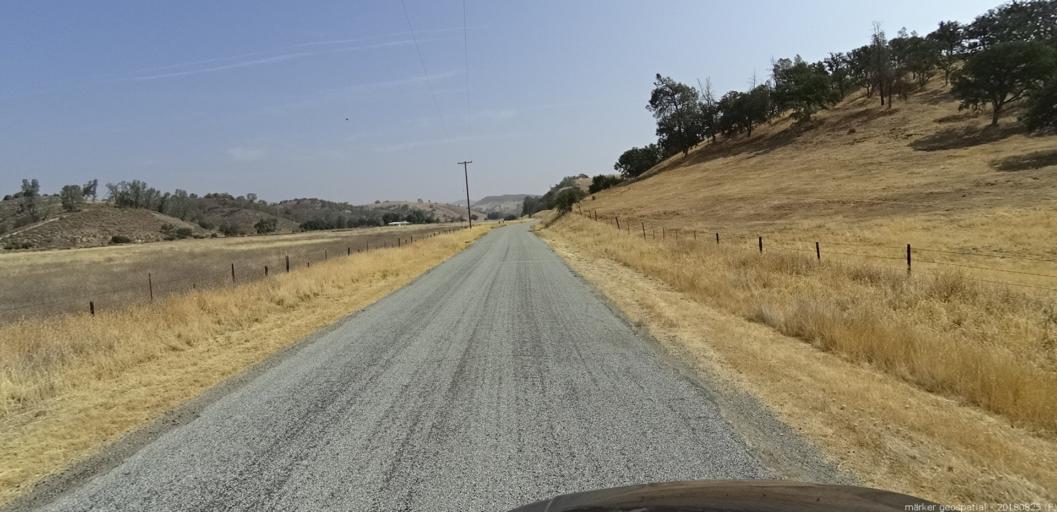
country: US
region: California
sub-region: San Luis Obispo County
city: San Miguel
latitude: 35.8460
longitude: -120.6135
